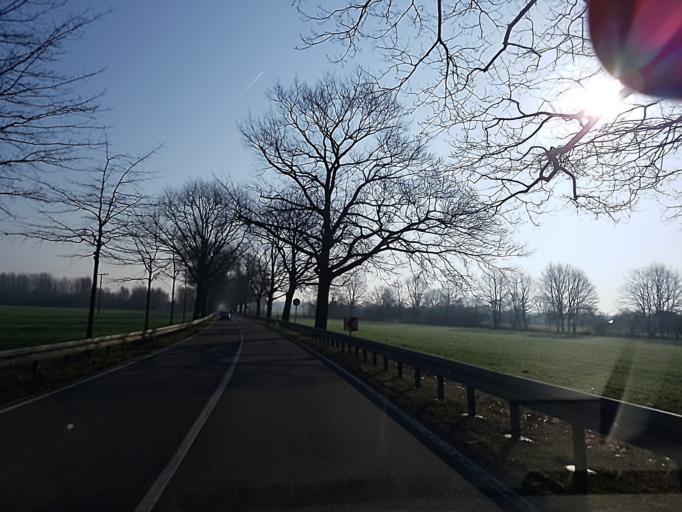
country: DE
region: Brandenburg
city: Vetschau
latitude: 51.7798
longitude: 14.0493
